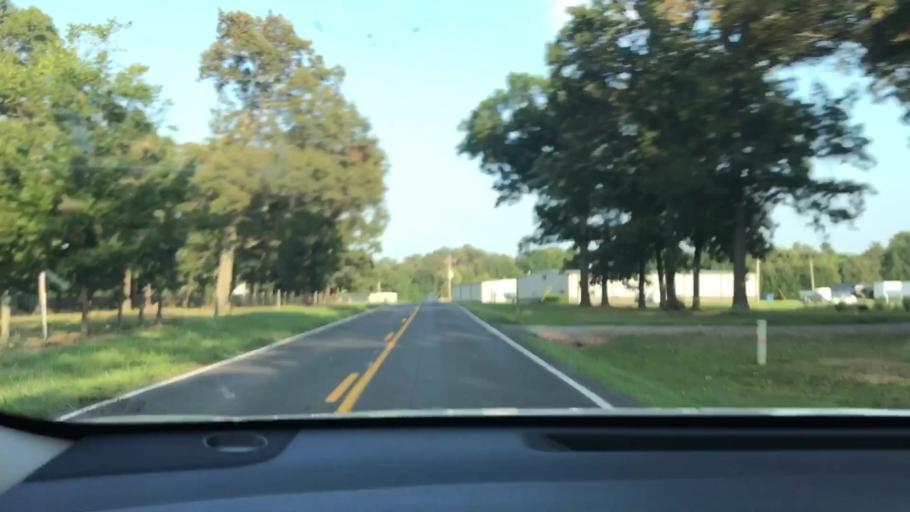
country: US
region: Kentucky
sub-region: Calloway County
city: Murray
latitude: 36.5812
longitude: -88.2773
